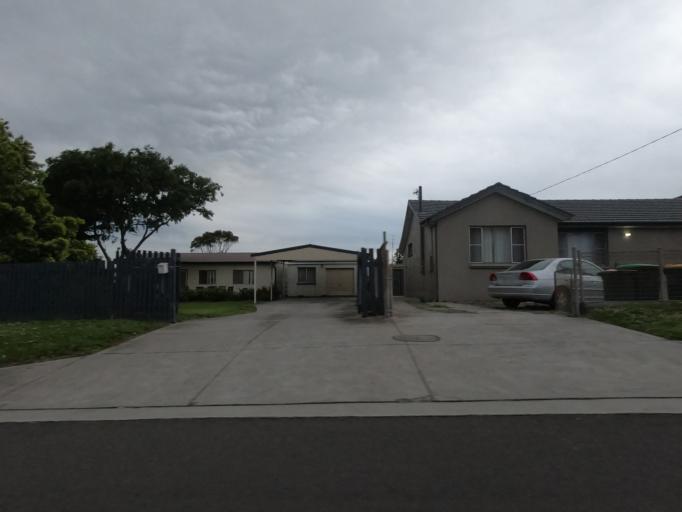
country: AU
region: New South Wales
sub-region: Wollongong
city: Lake Heights
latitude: -34.4830
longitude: 150.8641
